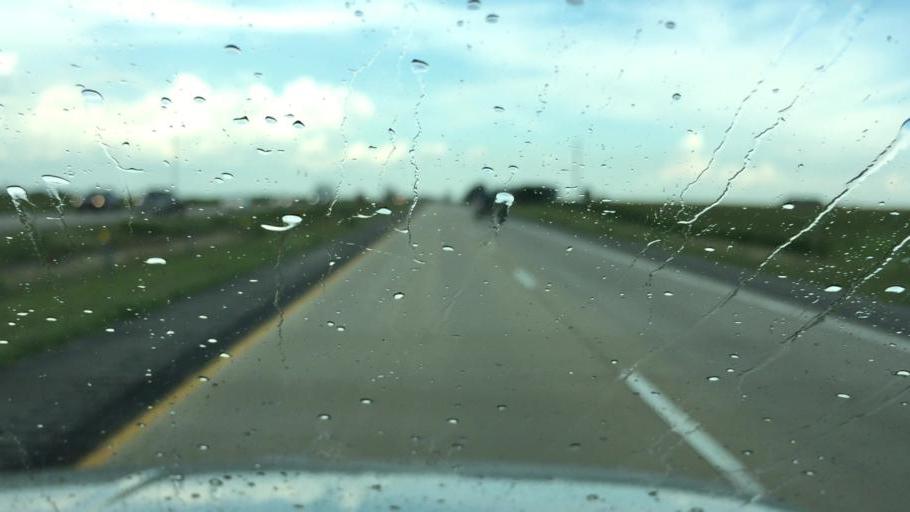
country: US
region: Iowa
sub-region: Poweshiek County
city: Brooklyn
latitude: 41.6961
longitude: -92.2722
